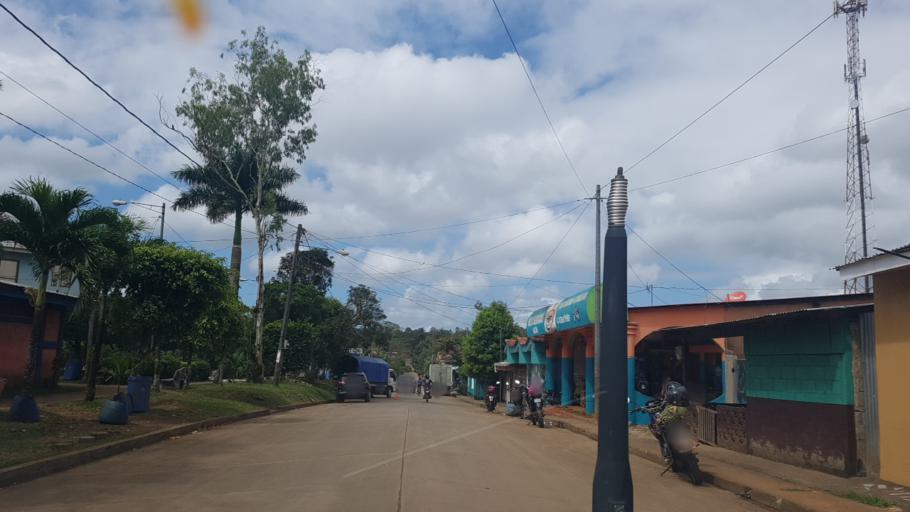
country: NI
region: Atlantico Sur
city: Nueva Guinea
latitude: 11.6891
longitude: -84.4577
